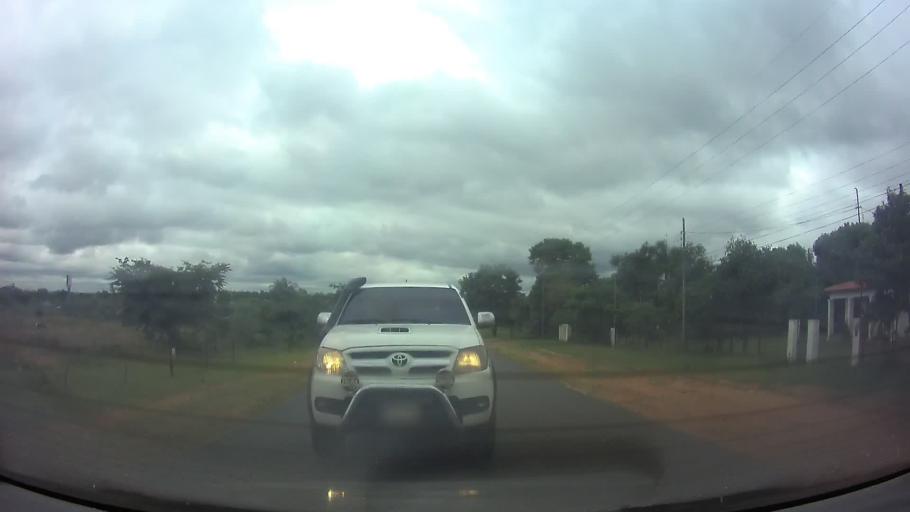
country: PY
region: Central
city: Guarambare
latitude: -25.5142
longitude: -57.4895
